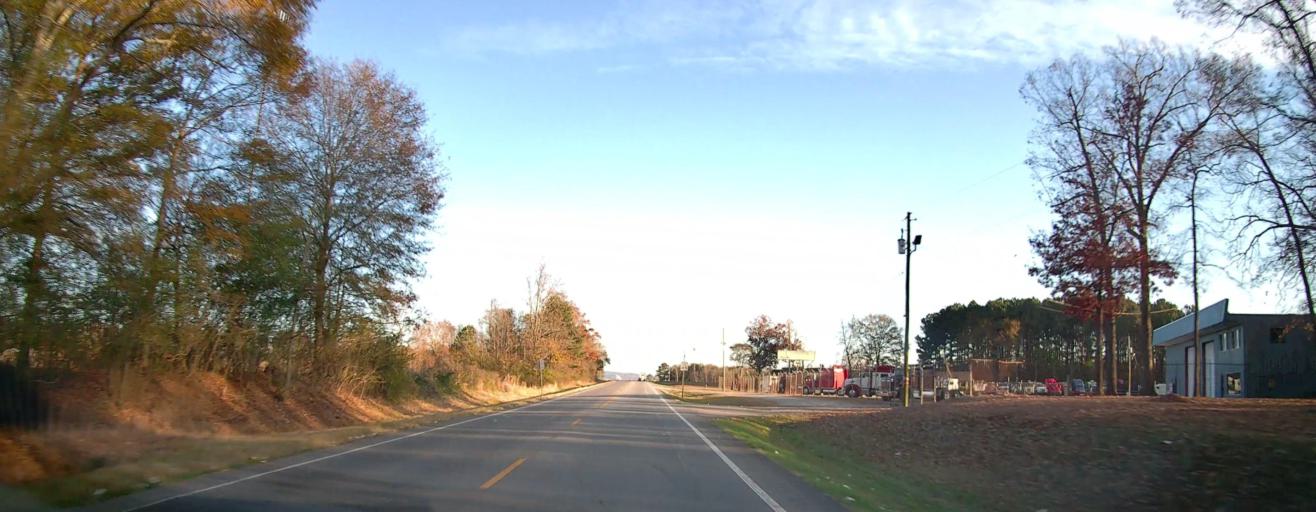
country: US
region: Alabama
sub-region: Blount County
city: Oneonta
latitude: 34.1244
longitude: -86.4025
